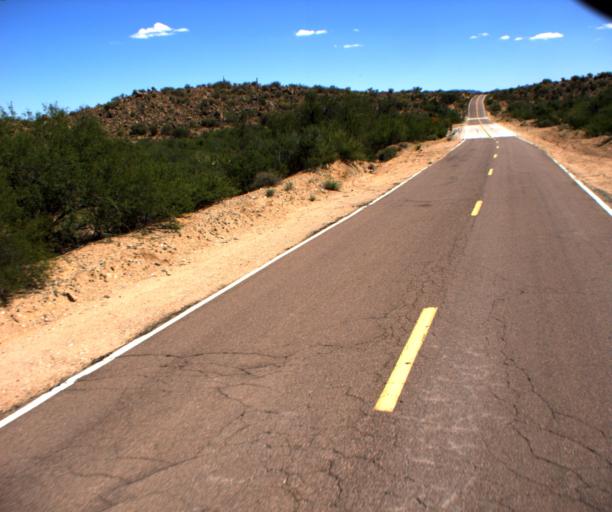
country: US
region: Arizona
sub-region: Yavapai County
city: Bagdad
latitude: 34.4439
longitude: -113.2420
